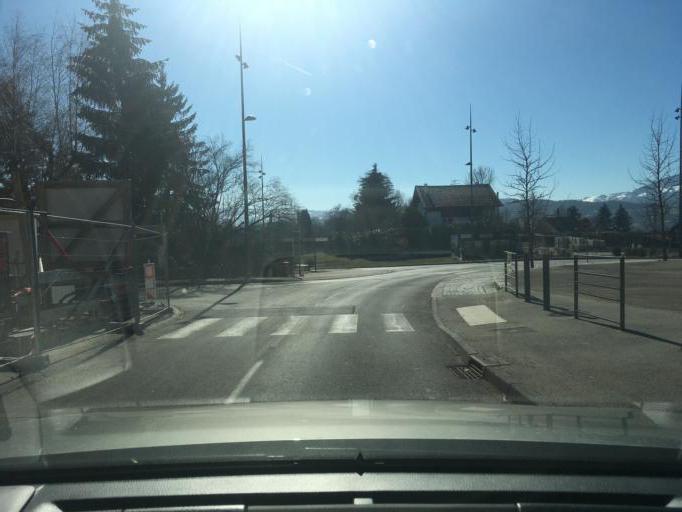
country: FR
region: Rhone-Alpes
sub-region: Departement de la Haute-Savoie
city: Vetraz-Monthoux
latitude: 46.1745
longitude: 6.2587
